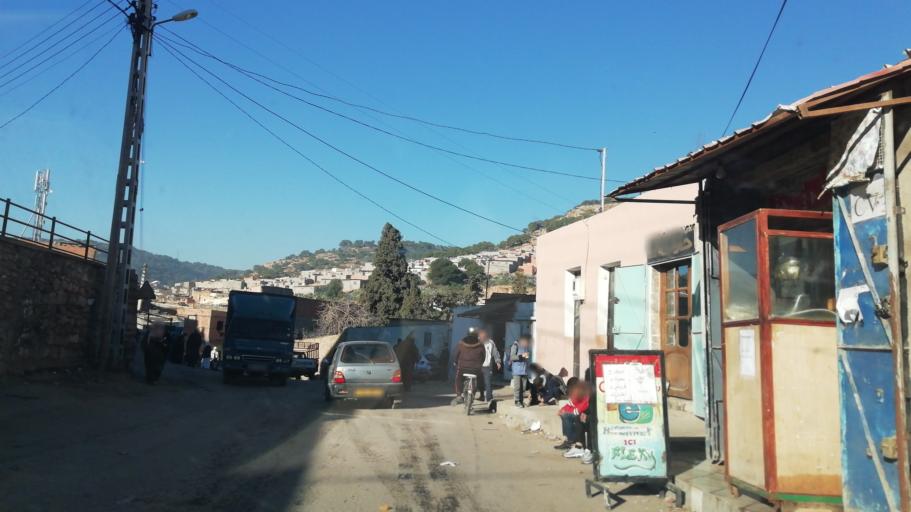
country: DZ
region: Oran
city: Oran
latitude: 35.6860
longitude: -0.6728
